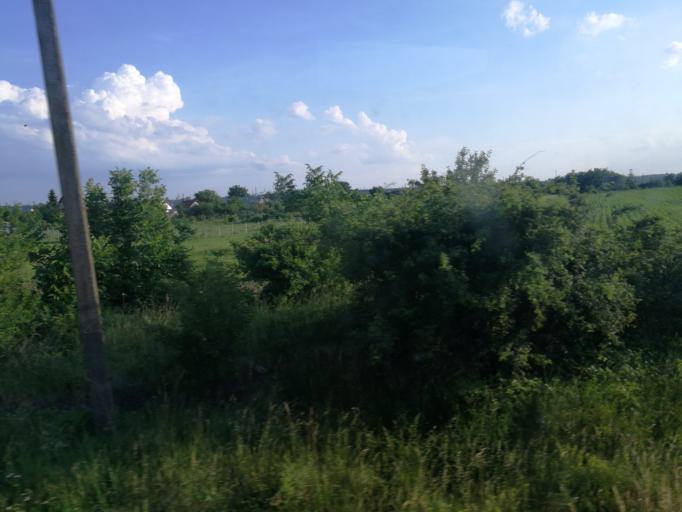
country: RO
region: Arges
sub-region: Oras Stefanesti
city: Golesti
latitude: 44.8378
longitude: 24.9554
